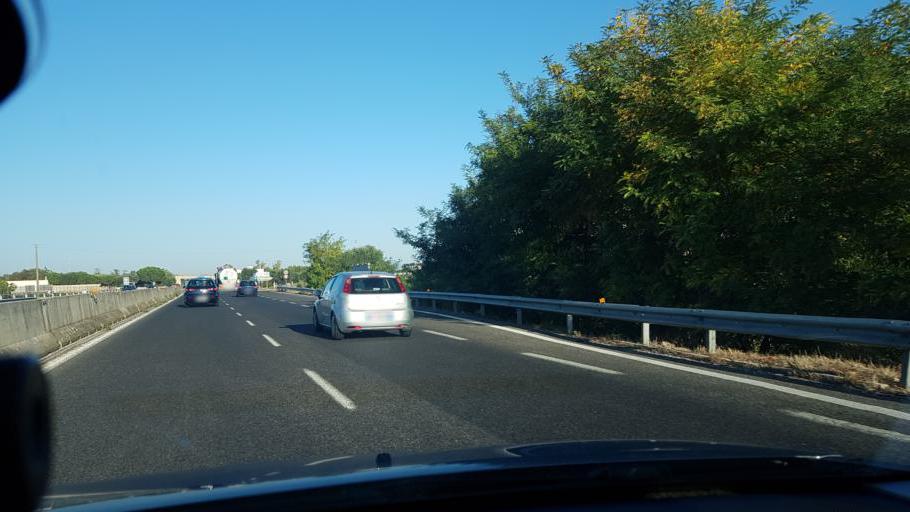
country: IT
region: Apulia
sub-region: Provincia di Bari
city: Monopoli
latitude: 40.9331
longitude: 17.2974
